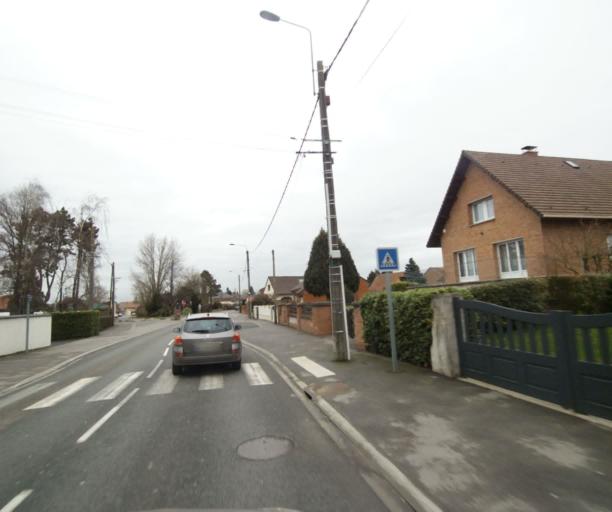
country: FR
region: Nord-Pas-de-Calais
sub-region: Departement du Nord
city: Aubry-du-Hainaut
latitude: 50.3711
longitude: 3.4592
